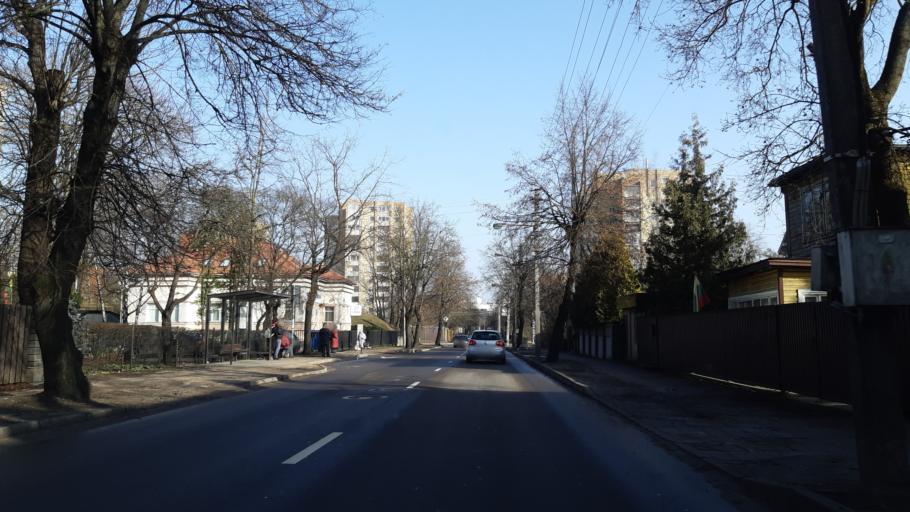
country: LT
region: Kauno apskritis
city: Dainava (Kaunas)
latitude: 54.9070
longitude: 23.9520
